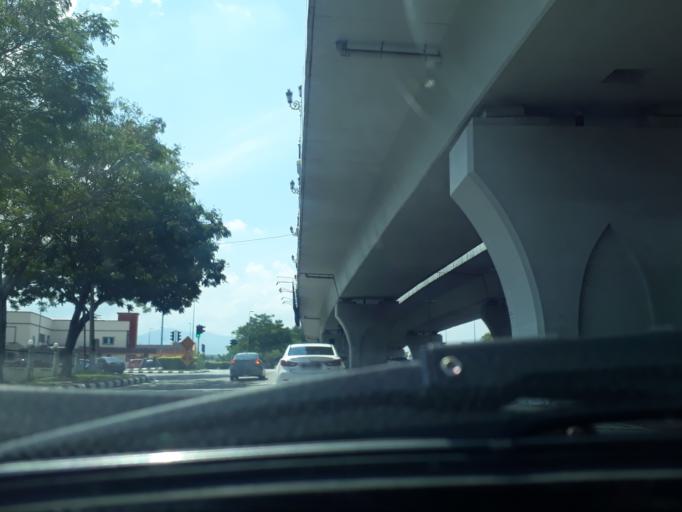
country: MY
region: Perak
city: Ipoh
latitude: 4.6018
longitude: 101.1191
